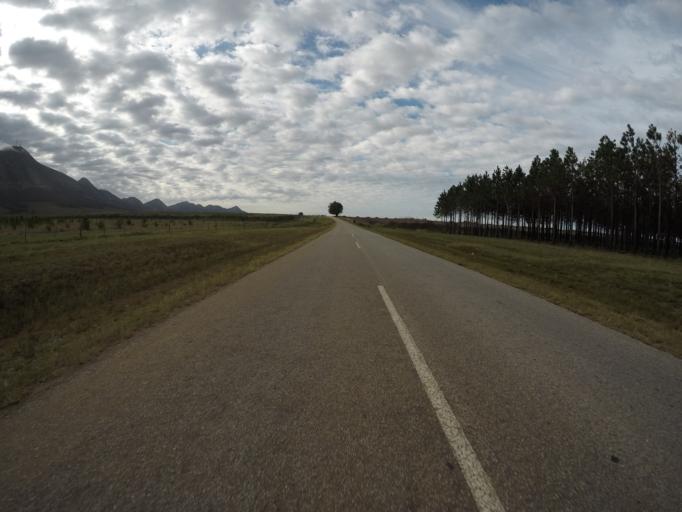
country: ZA
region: Eastern Cape
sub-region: Cacadu District Municipality
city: Kareedouw
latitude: -34.0400
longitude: 24.4055
